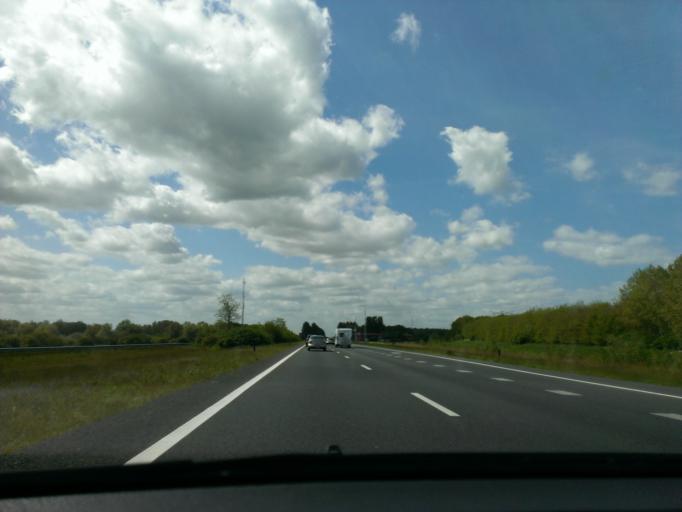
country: NL
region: Flevoland
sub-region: Gemeente Lelystad
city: Lelystad
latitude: 52.4385
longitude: 5.4304
